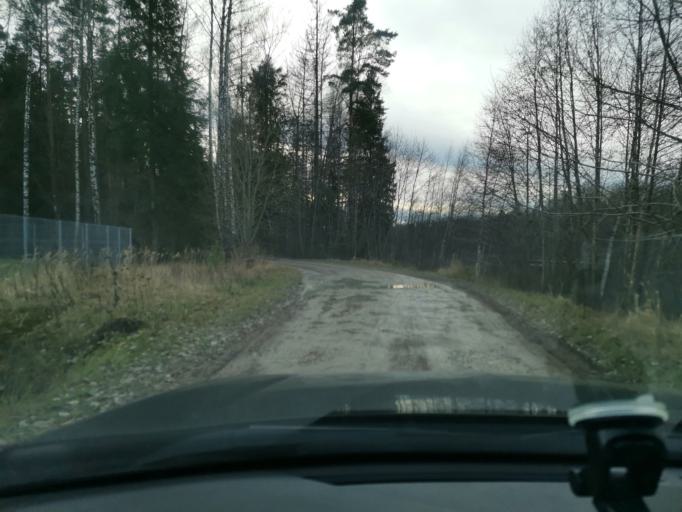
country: EE
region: Ida-Virumaa
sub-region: Sillamaee linn
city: Sillamae
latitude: 59.2576
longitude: 27.9149
